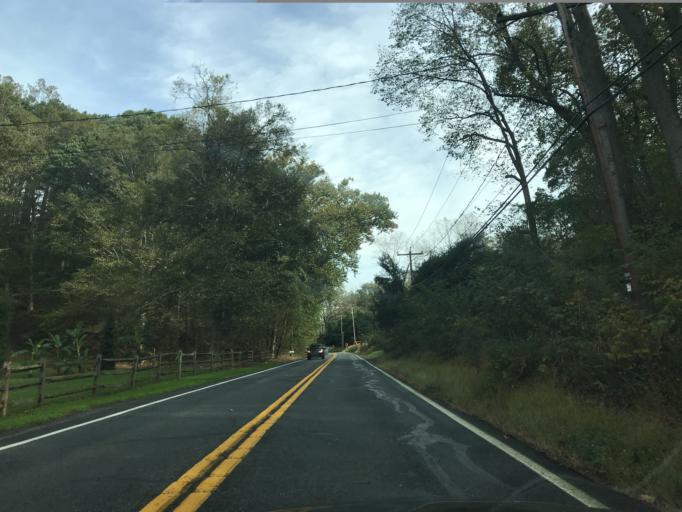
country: US
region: Maryland
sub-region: Harford County
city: Pleasant Hills
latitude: 39.4803
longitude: -76.4182
